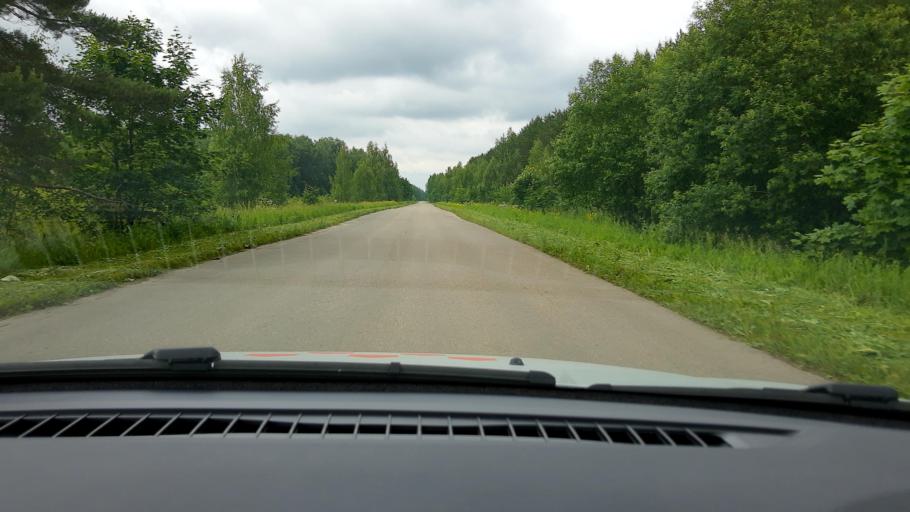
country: RU
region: Nizjnij Novgorod
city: Bogorodsk
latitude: 56.0382
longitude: 43.4708
